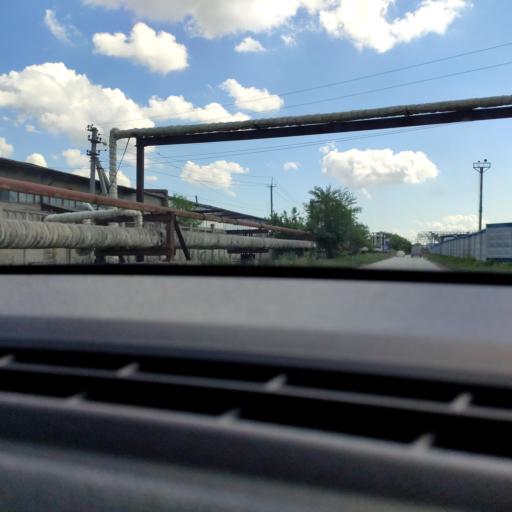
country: RU
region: Samara
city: Tol'yatti
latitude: 53.5779
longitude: 49.2780
